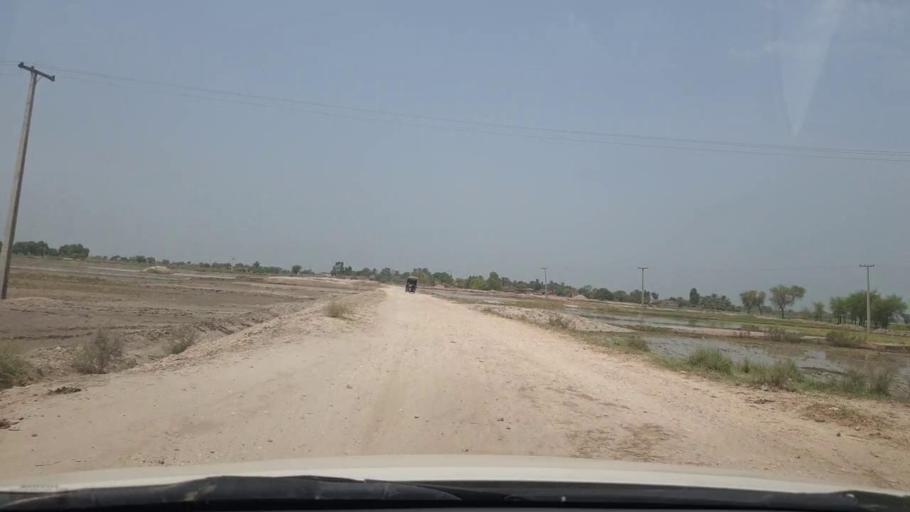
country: PK
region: Sindh
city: Rustam jo Goth
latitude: 28.0385
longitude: 68.7545
